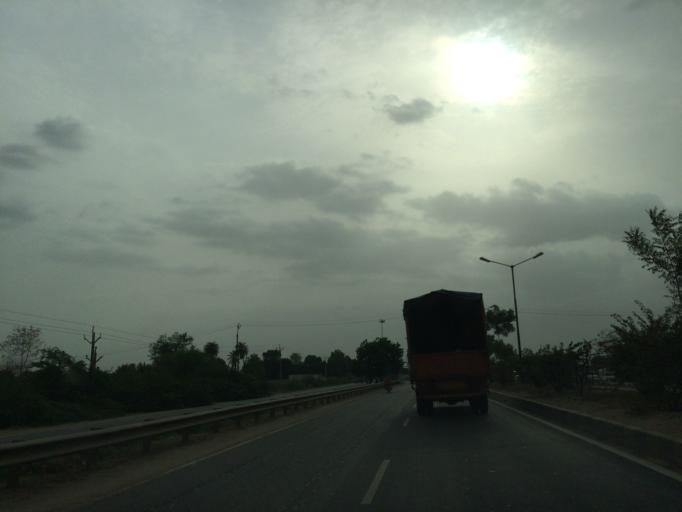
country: IN
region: Gujarat
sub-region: Ahmadabad
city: Sarkhej
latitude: 22.9344
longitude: 72.5230
